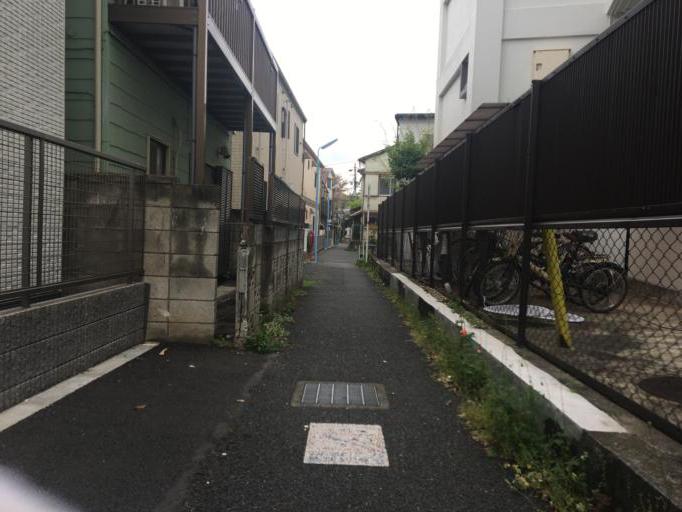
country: JP
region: Tokyo
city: Tokyo
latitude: 35.6969
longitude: 139.6502
